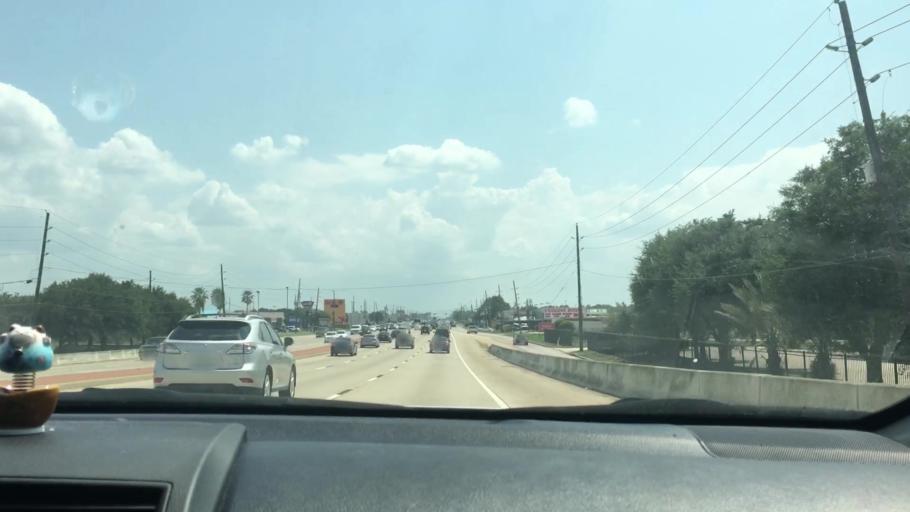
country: US
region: Texas
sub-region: Fort Bend County
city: Mission Bend
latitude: 29.7088
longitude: -95.6442
